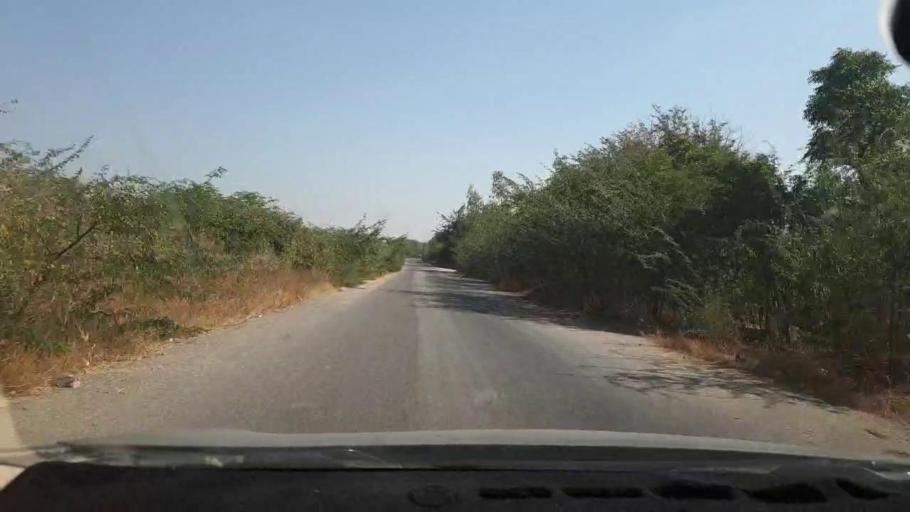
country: PK
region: Sindh
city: Malir Cantonment
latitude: 25.1417
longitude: 67.1975
